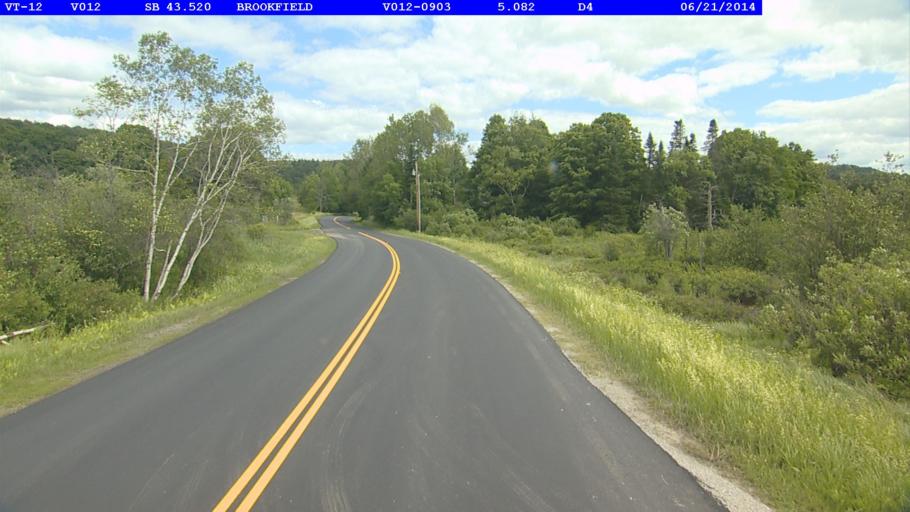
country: US
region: Vermont
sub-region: Washington County
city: Northfield
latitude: 44.0726
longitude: -72.6366
